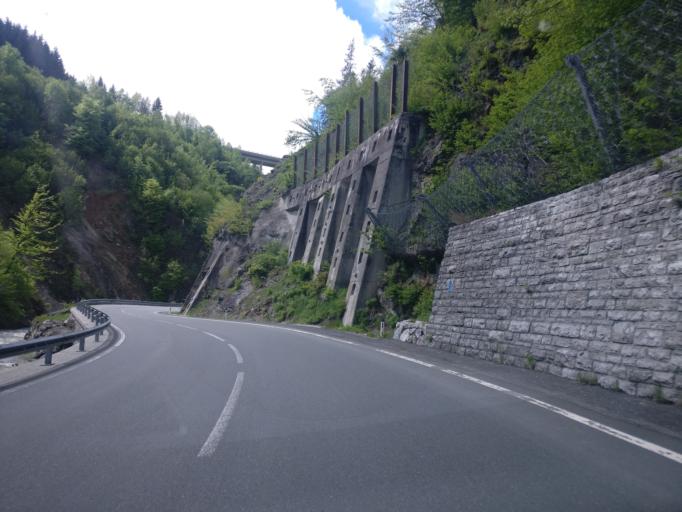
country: AT
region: Salzburg
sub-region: Politischer Bezirk Sankt Johann im Pongau
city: Bischofshofen
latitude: 47.4352
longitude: 13.2289
